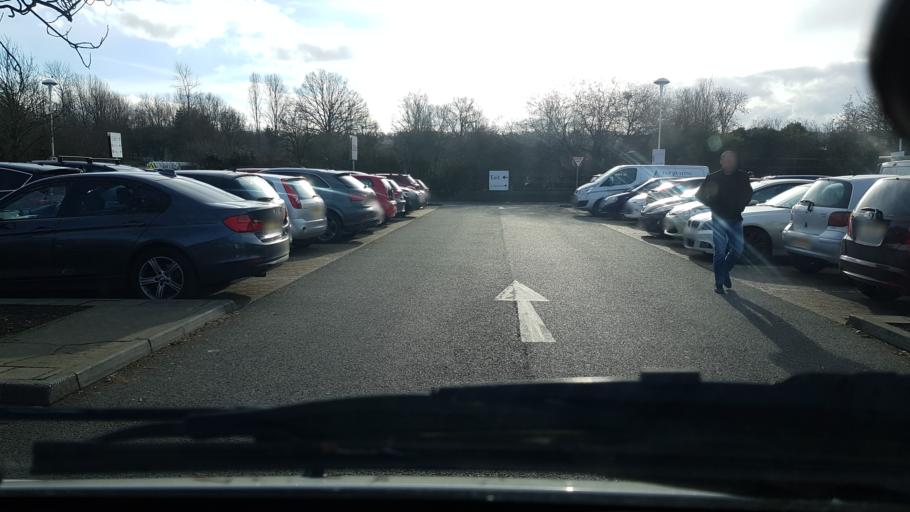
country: GB
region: England
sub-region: Surrey
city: Guildford
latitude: 51.2416
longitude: -0.6042
